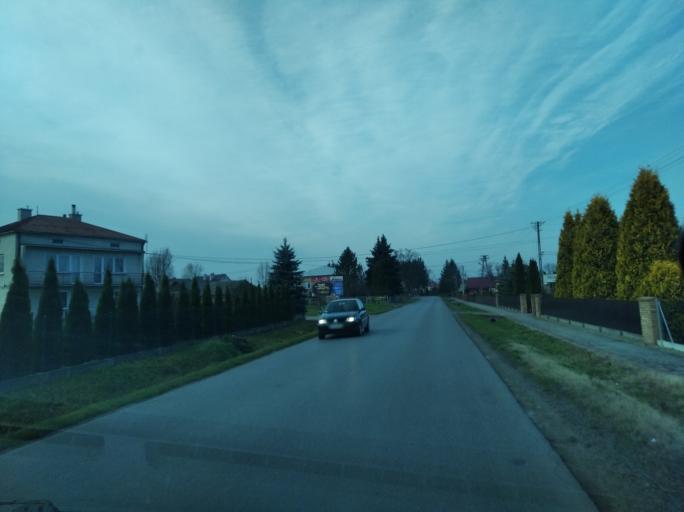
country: PL
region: Subcarpathian Voivodeship
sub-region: Powiat ropczycko-sedziszowski
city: Iwierzyce
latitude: 50.0527
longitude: 21.7452
